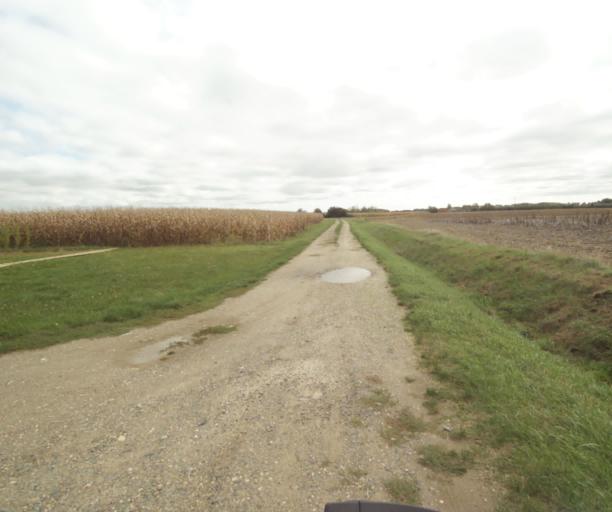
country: FR
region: Midi-Pyrenees
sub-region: Departement du Tarn-et-Garonne
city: Montech
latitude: 43.9717
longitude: 1.2001
